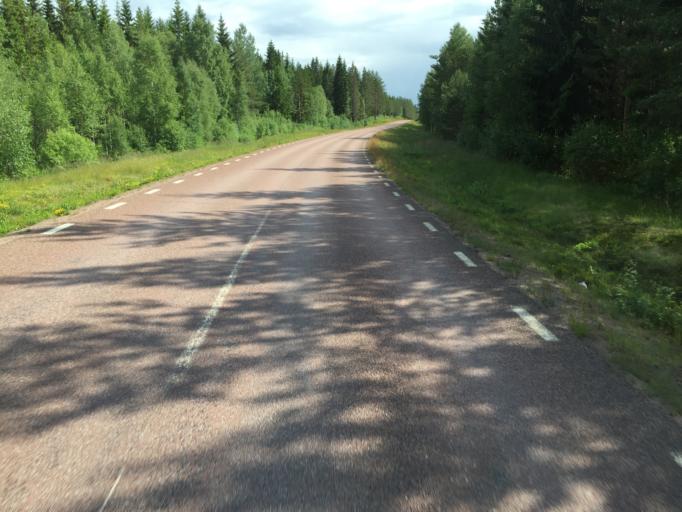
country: SE
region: Dalarna
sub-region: Vansbro Kommun
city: Vansbro
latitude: 60.6369
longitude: 14.1493
